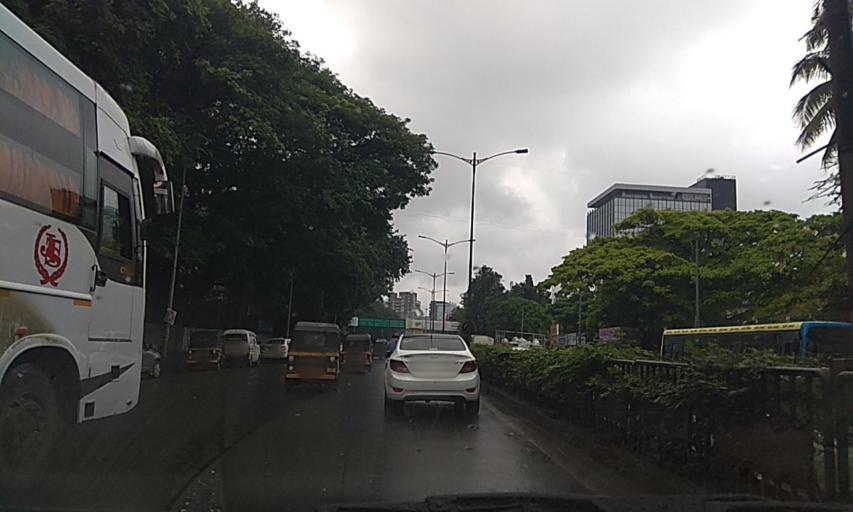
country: IN
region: Maharashtra
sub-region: Pune Division
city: Shivaji Nagar
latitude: 18.5305
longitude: 73.8485
